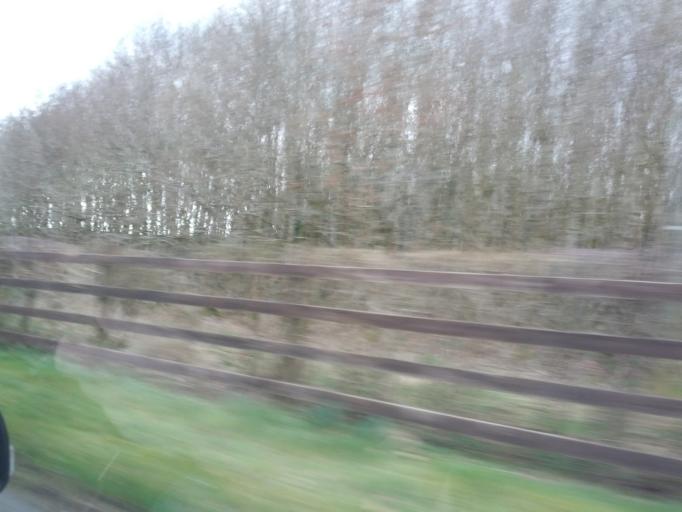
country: IE
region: Connaught
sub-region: County Galway
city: Athenry
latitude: 53.3765
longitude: -8.6283
